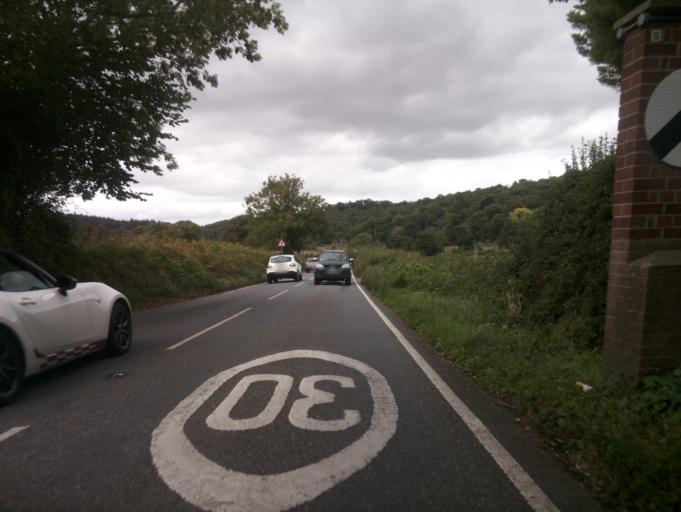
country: GB
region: England
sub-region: Devon
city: Starcross
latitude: 50.6441
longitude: -3.4769
